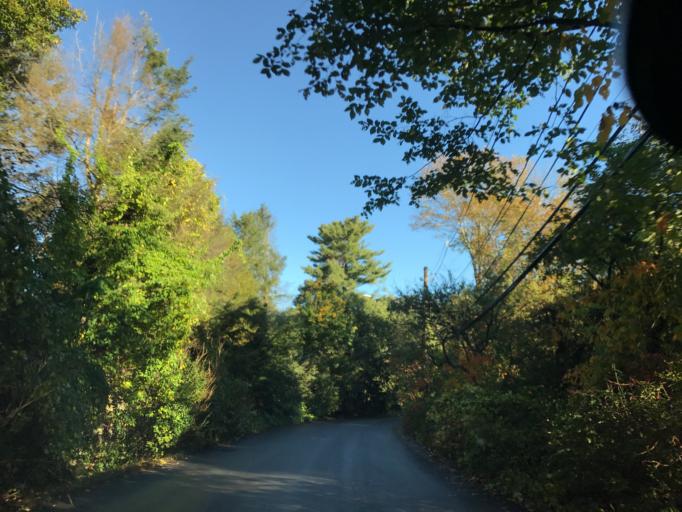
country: US
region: Massachusetts
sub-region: Middlesex County
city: Newton
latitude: 42.3107
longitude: -71.1816
